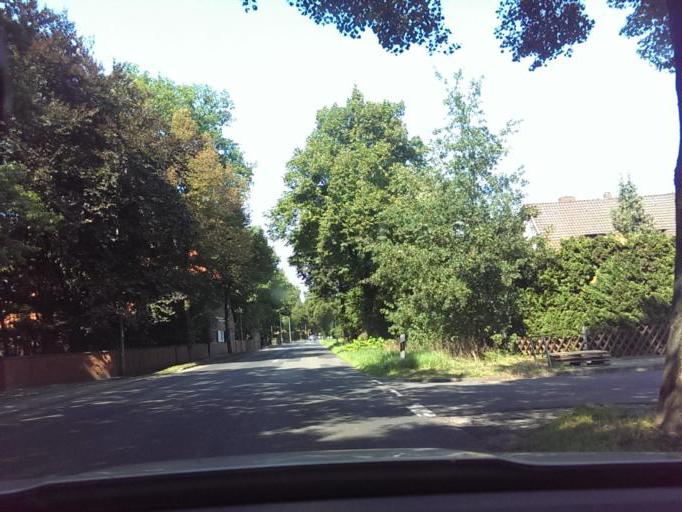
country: DE
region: Lower Saxony
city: Langenhagen
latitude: 52.4616
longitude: 9.7888
